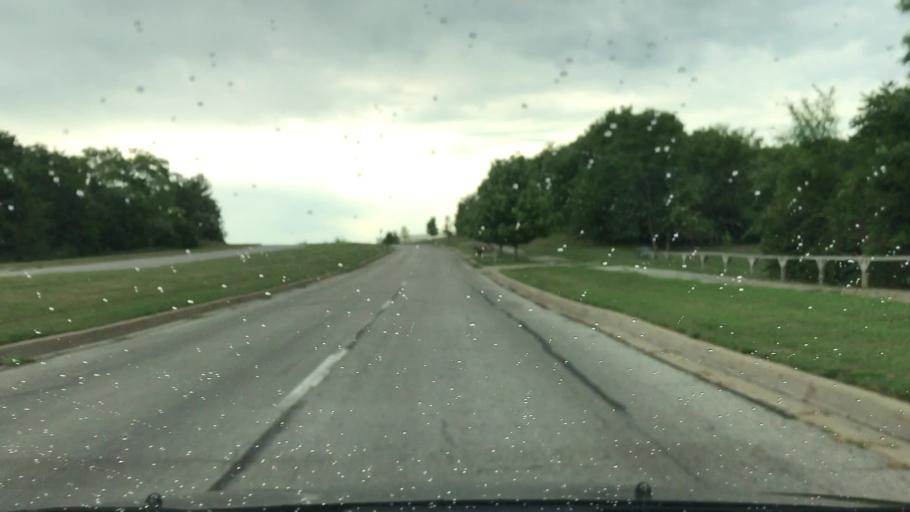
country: US
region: Missouri
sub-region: Jackson County
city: Grandview
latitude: 38.9261
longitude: -94.4859
